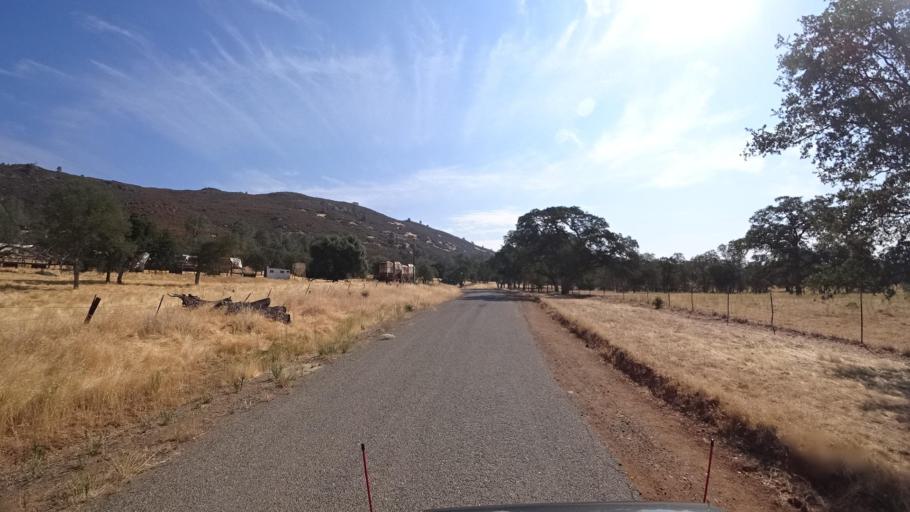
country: US
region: California
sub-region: Tuolumne County
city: Tuolumne City
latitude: 37.7219
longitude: -120.2933
